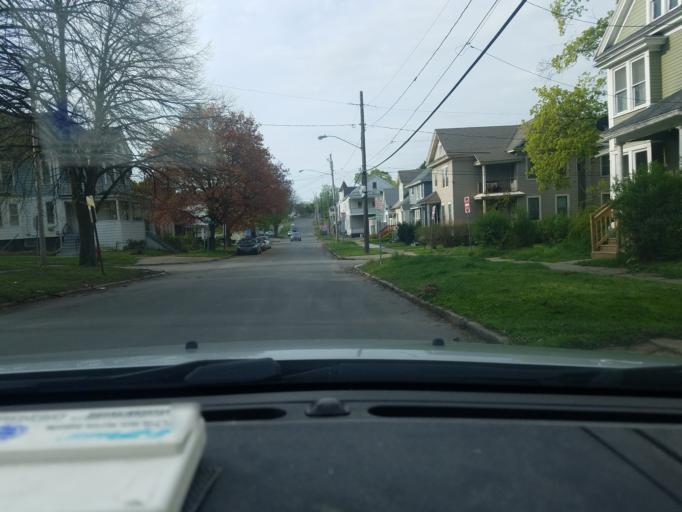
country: US
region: New York
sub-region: Onondaga County
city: Syracuse
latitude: 43.0624
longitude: -76.1414
